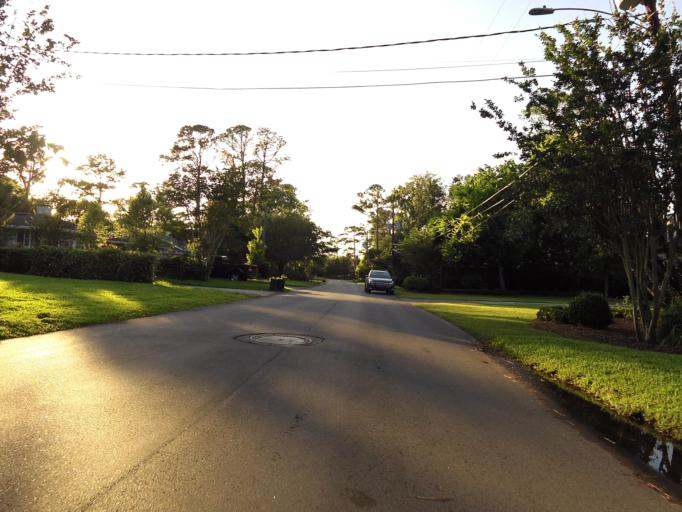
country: US
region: Florida
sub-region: Duval County
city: Jacksonville
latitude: 30.2553
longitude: -81.6916
